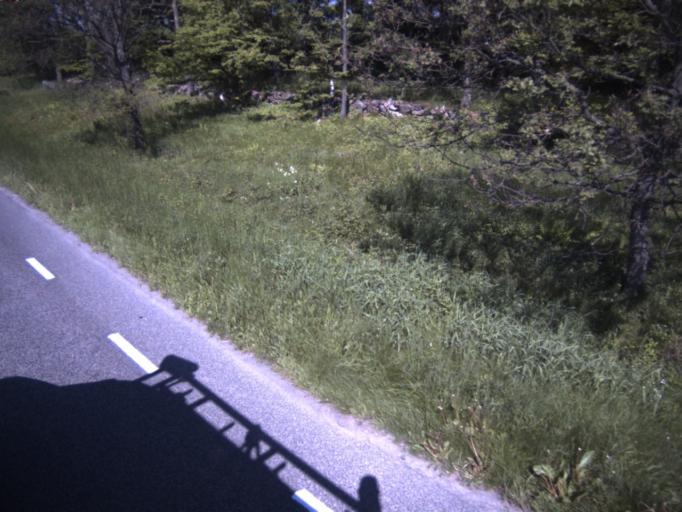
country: SE
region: Skane
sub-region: Helsingborg
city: Odakra
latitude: 56.0573
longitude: 12.7721
